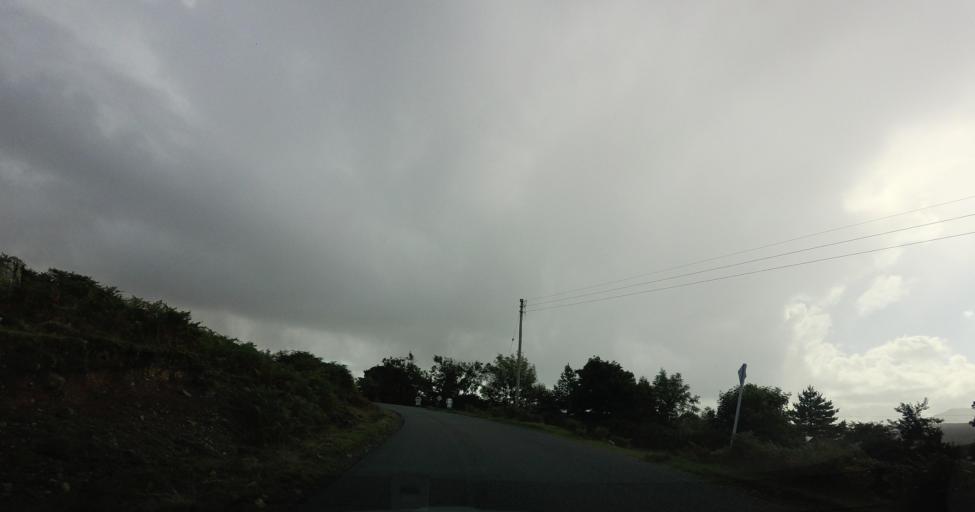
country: GB
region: Scotland
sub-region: Highland
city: Portree
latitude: 57.2116
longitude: -6.0080
